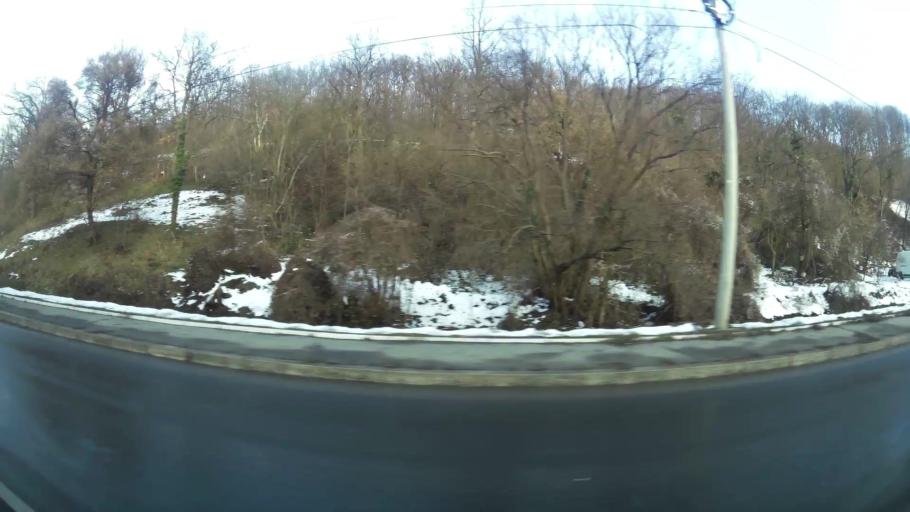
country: RS
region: Central Serbia
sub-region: Belgrade
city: Rakovica
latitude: 44.7308
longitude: 20.4476
